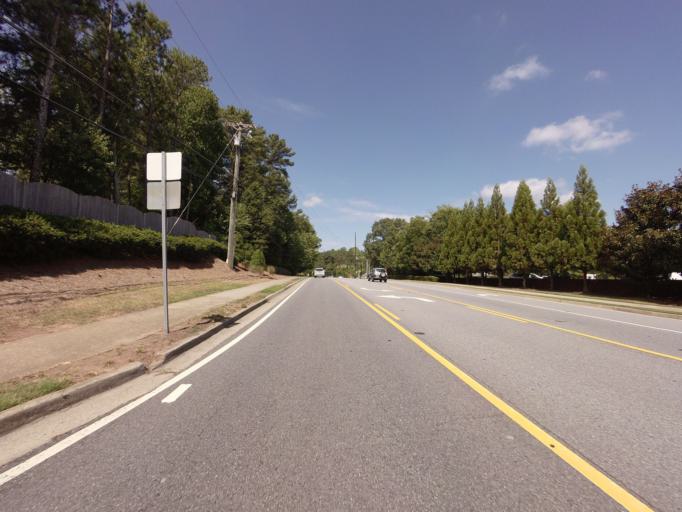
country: US
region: Georgia
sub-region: Fulton County
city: Johns Creek
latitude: 34.0688
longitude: -84.2052
